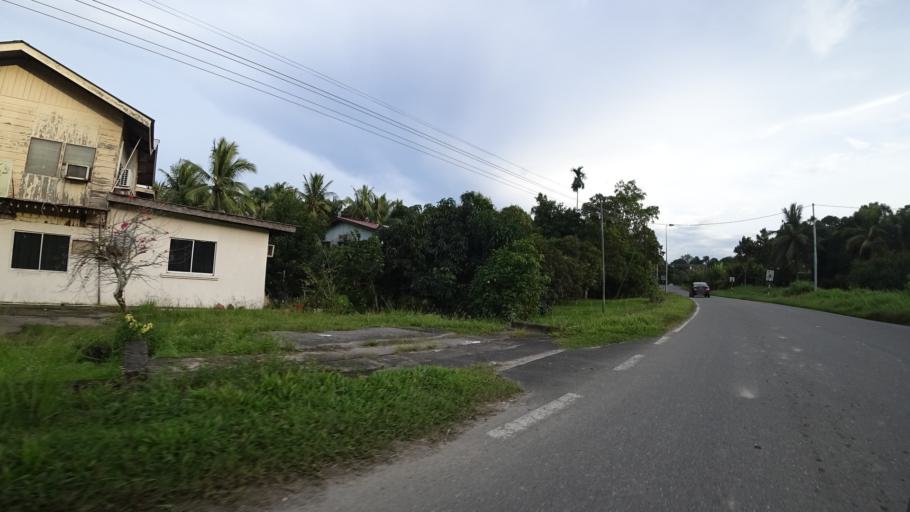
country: BN
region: Brunei and Muara
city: Bandar Seri Begawan
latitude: 4.8554
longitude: 114.8211
